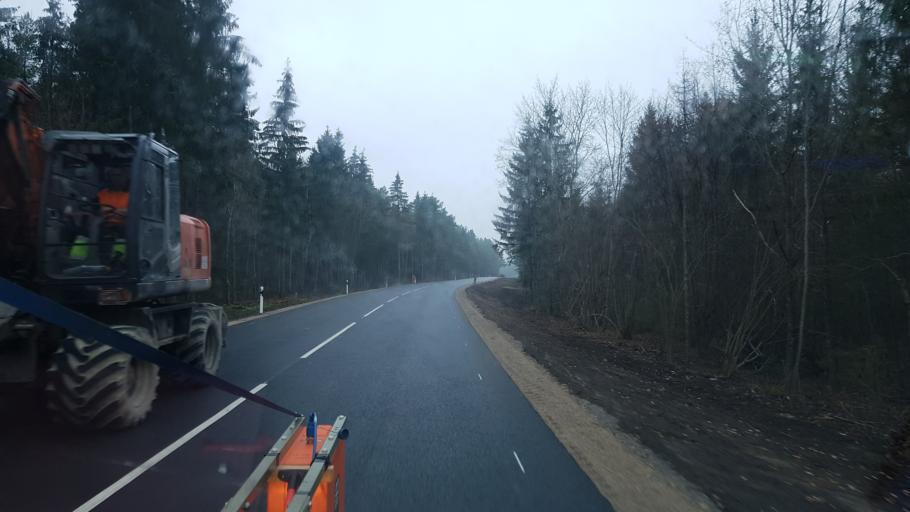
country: EE
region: Raplamaa
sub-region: Kohila vald
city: Kohila
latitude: 59.1778
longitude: 24.7898
